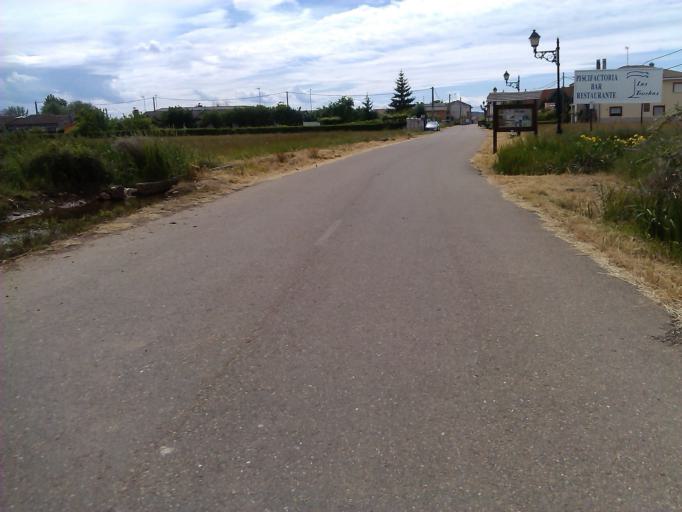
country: ES
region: Castille and Leon
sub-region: Provincia de Leon
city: Hospital de Orbigo
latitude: 42.4640
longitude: -5.8736
